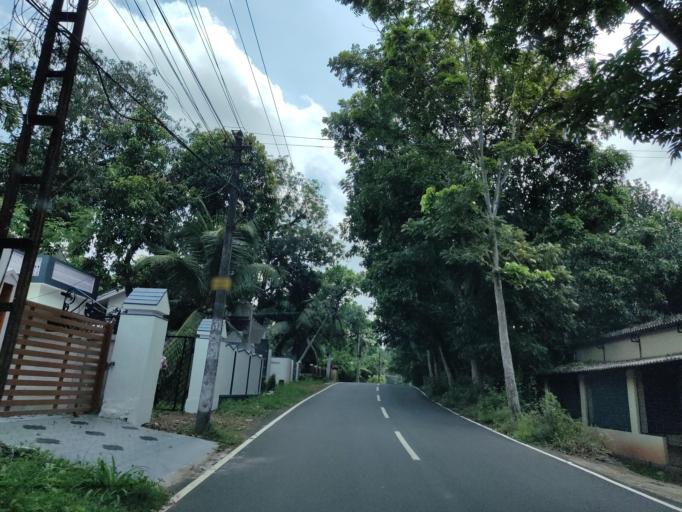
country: IN
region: Kerala
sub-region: Alappuzha
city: Mavelikara
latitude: 9.2656
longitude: 76.5607
